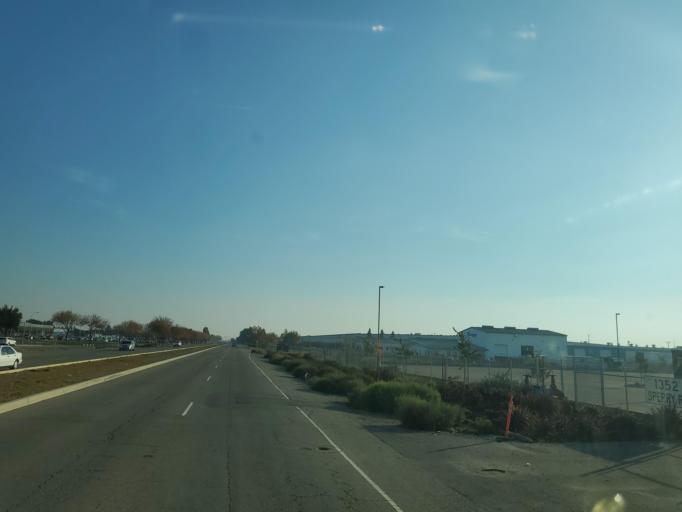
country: US
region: California
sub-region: San Joaquin County
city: French Camp
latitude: 37.8996
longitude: -121.2540
